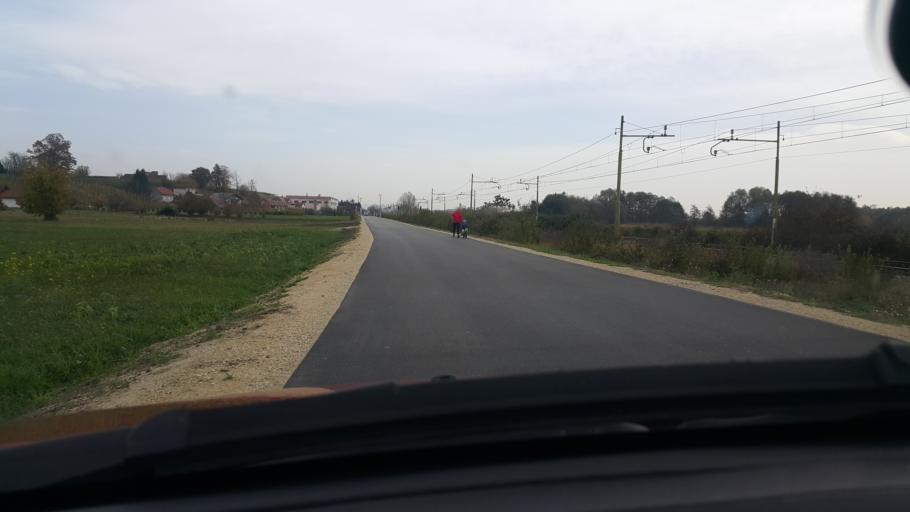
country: SI
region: Brezice
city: Brezice
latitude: 45.9041
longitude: 15.6375
